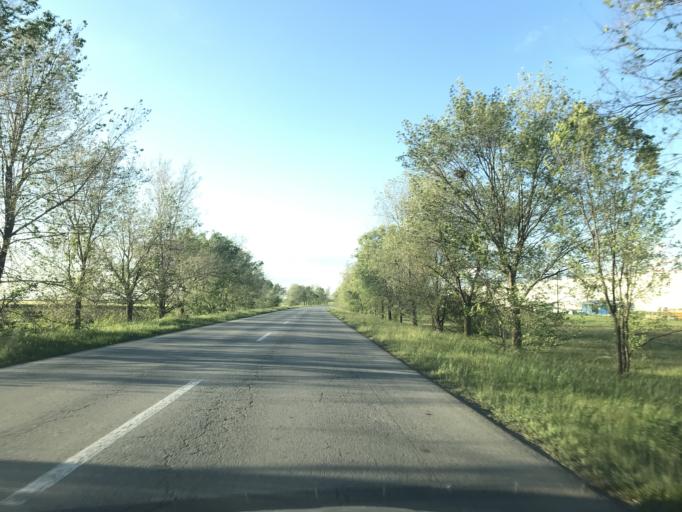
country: RS
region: Autonomna Pokrajina Vojvodina
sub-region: Srednjebanatski Okrug
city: Zrenjanin
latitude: 45.3871
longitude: 20.3521
